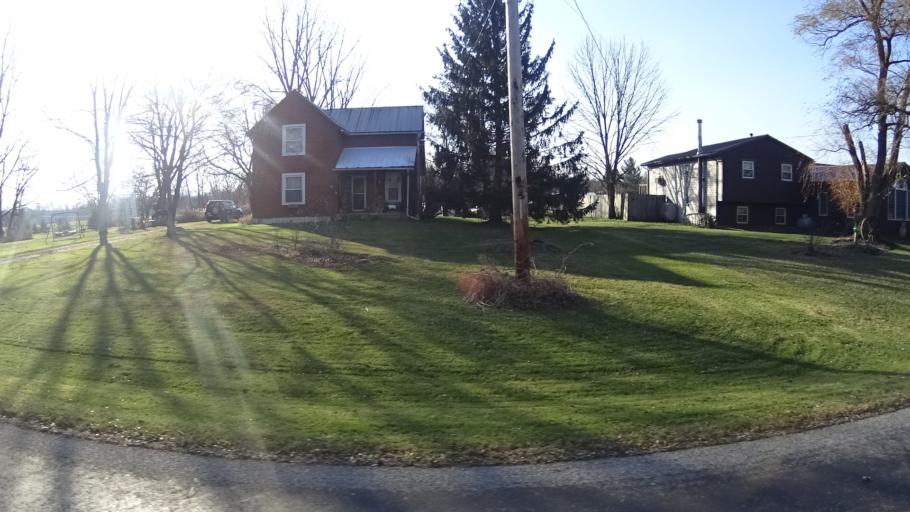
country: US
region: Ohio
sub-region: Lorain County
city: Oberlin
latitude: 41.2652
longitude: -82.1897
